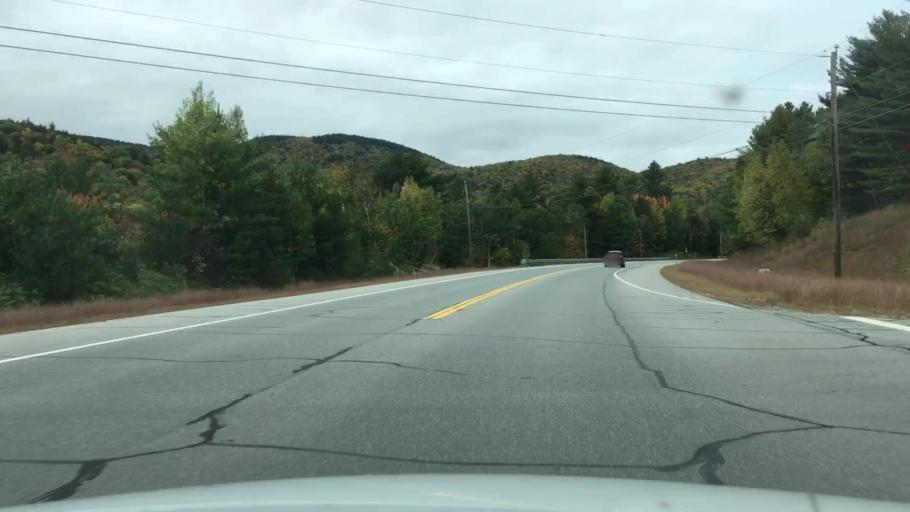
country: US
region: New Hampshire
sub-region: Coos County
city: Gorham
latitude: 44.3970
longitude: -71.0655
